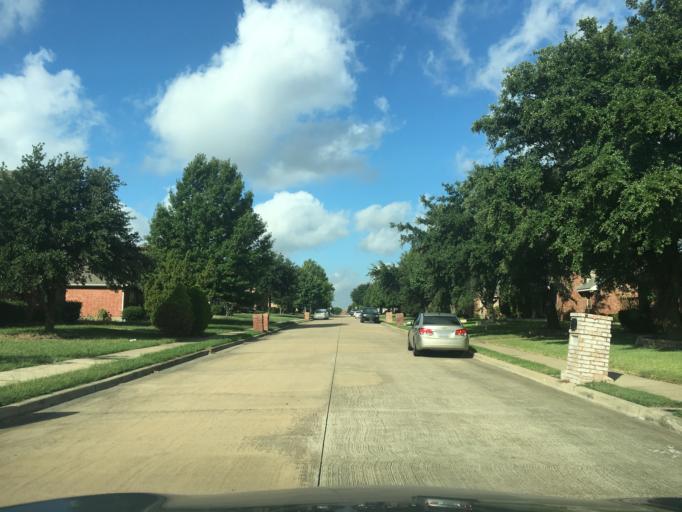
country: US
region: Texas
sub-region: Dallas County
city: Sachse
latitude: 32.9631
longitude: -96.5768
